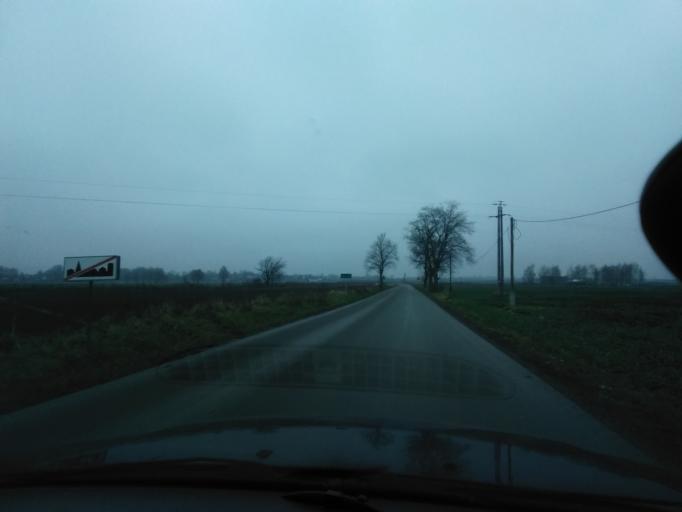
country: PL
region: Subcarpathian Voivodeship
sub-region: Powiat przeworski
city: Urzejowice
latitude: 50.0059
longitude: 22.4770
